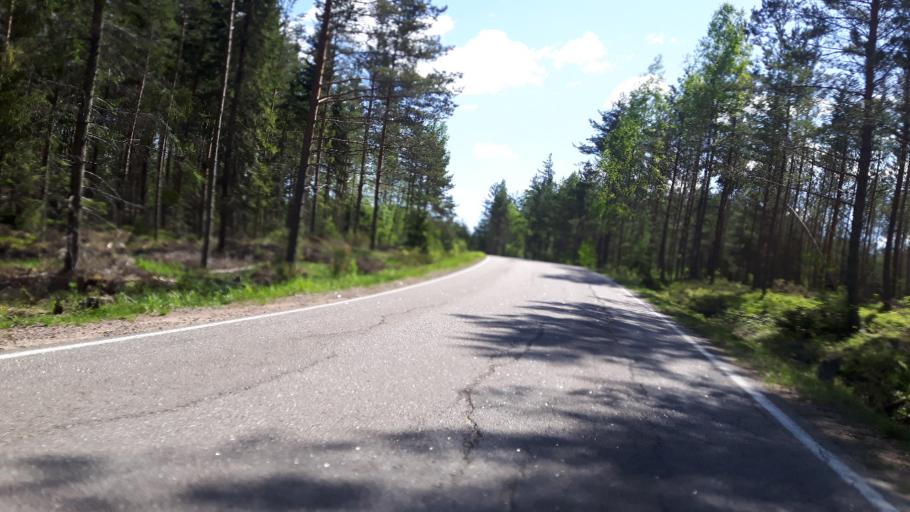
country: FI
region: Kymenlaakso
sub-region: Kotka-Hamina
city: Hamina
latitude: 60.5133
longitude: 27.3908
